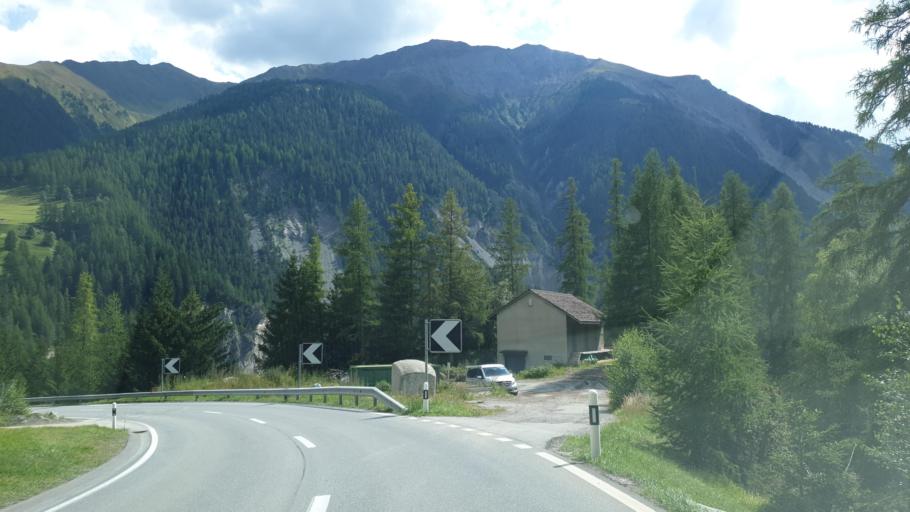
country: CH
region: Grisons
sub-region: Plessur District
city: Arosa
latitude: 46.6996
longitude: 9.7147
